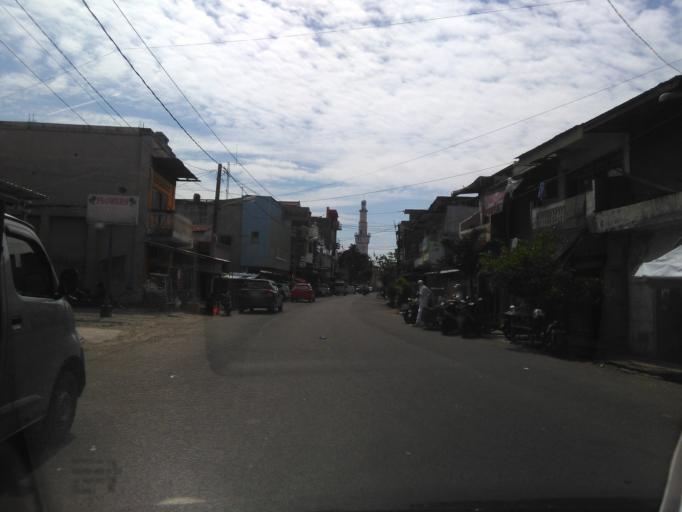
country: ID
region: South Sulawesi
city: Parepare
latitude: -4.0171
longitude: 119.6217
